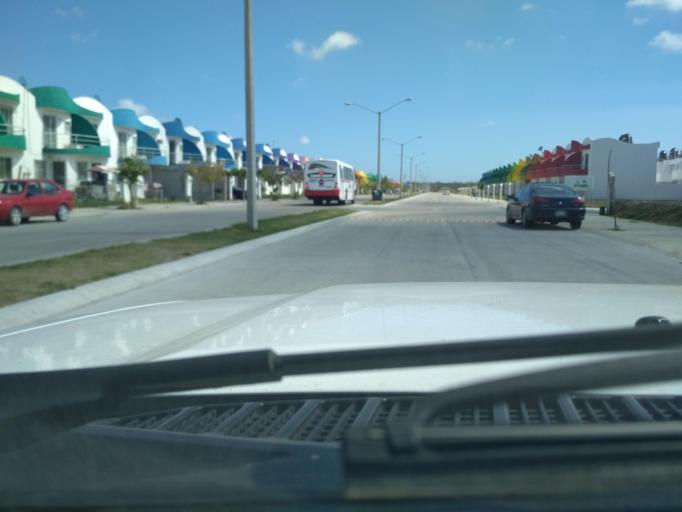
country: MX
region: Veracruz
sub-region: Veracruz
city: Las Amapolas
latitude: 19.1335
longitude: -96.2090
